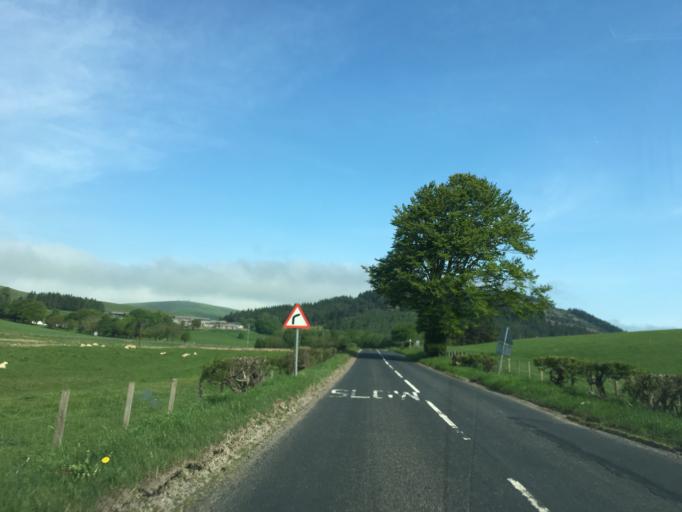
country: GB
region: Scotland
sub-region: South Lanarkshire
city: Biggar
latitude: 55.6509
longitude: -3.4332
